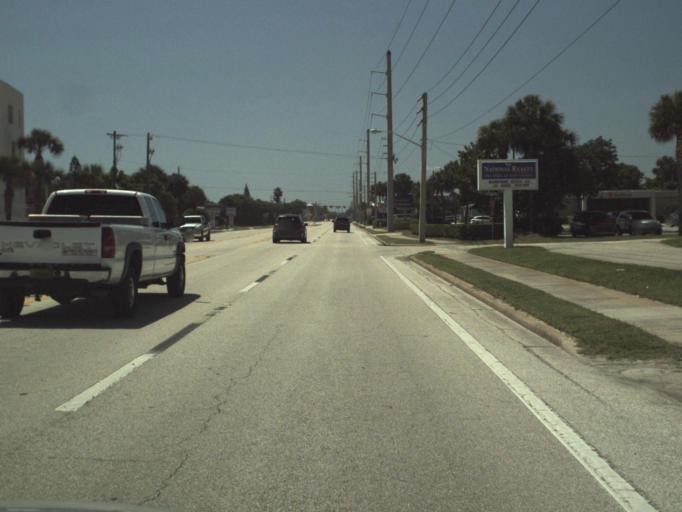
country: US
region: Florida
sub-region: Brevard County
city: Indialantic
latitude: 28.0955
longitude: -80.5682
